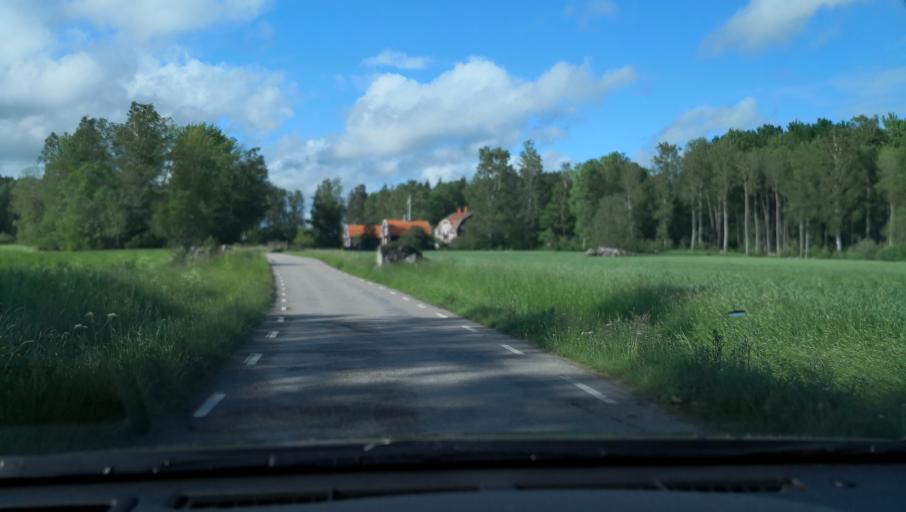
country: SE
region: OErebro
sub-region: Lindesbergs Kommun
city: Fellingsbro
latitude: 59.3393
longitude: 15.6871
